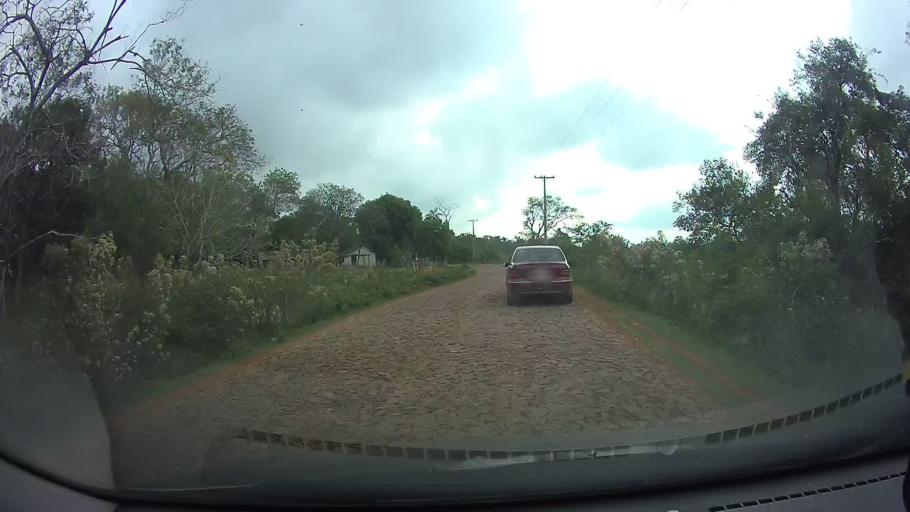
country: PY
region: Cordillera
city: Arroyos y Esteros
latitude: -25.0163
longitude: -57.1208
